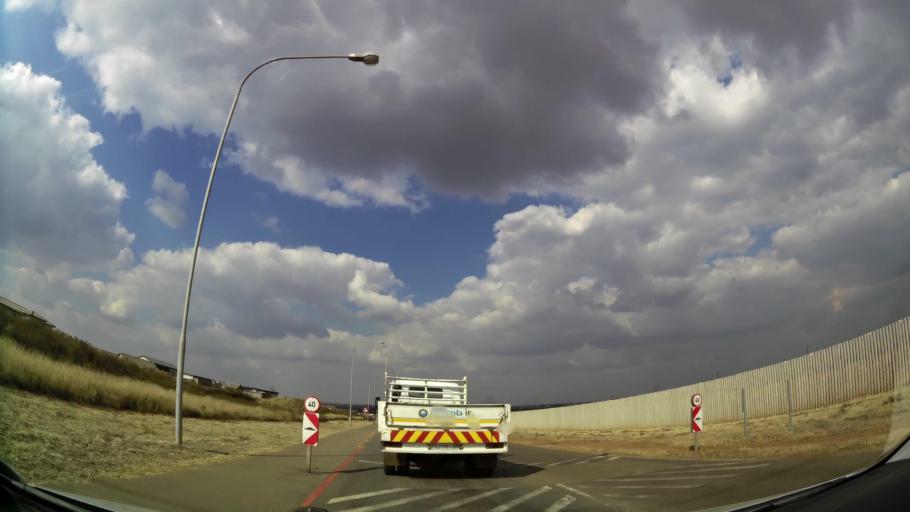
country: ZA
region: Gauteng
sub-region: Ekurhuleni Metropolitan Municipality
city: Tembisa
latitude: -25.9291
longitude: 28.2035
